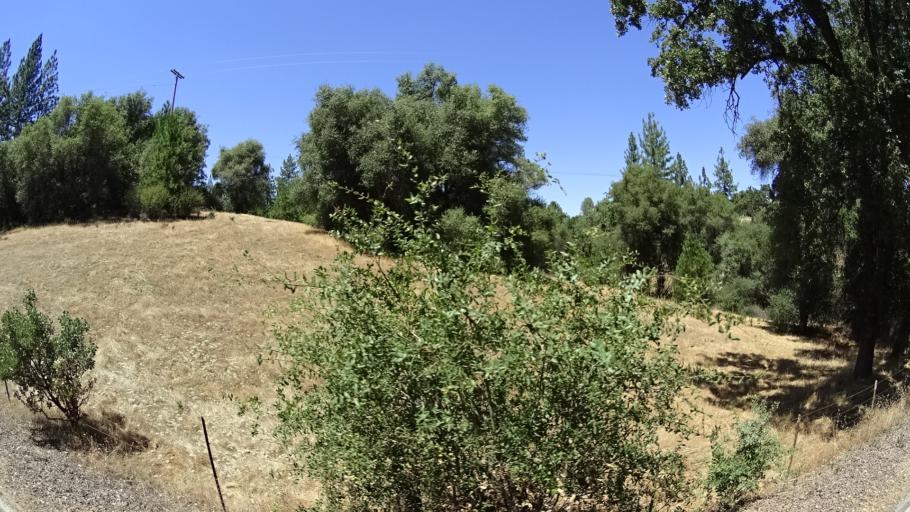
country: US
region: California
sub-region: Calaveras County
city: Angels Camp
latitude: 38.1135
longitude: -120.5192
